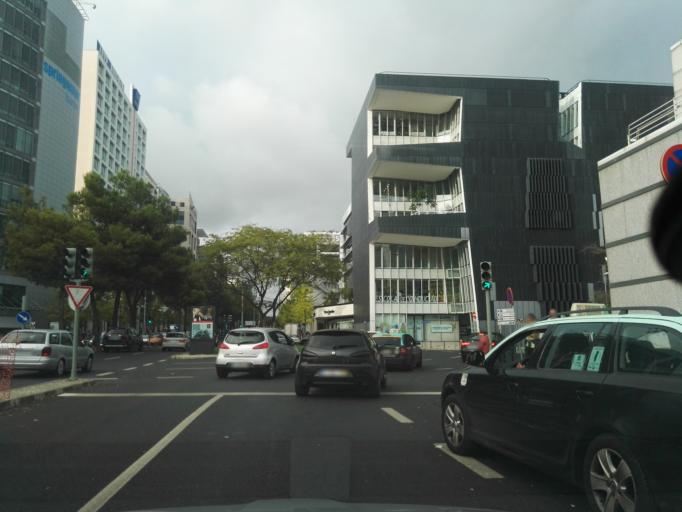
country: PT
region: Lisbon
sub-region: Loures
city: Moscavide
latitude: 38.7682
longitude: -9.0977
